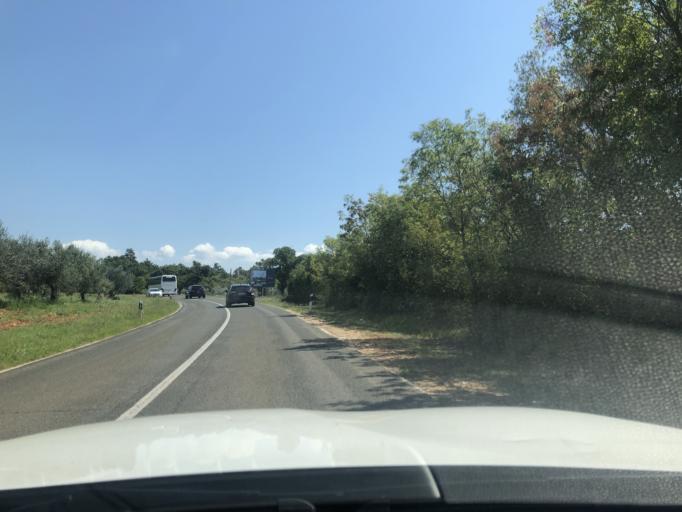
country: HR
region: Istarska
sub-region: Grad Rovinj
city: Rovinj
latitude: 45.0413
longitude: 13.7564
